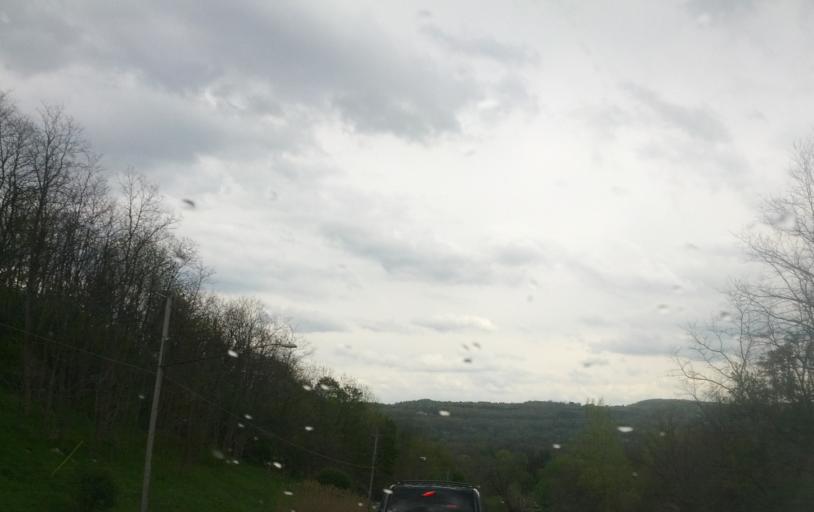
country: US
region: New York
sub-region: Onondaga County
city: Nedrow
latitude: 43.0048
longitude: -76.1628
